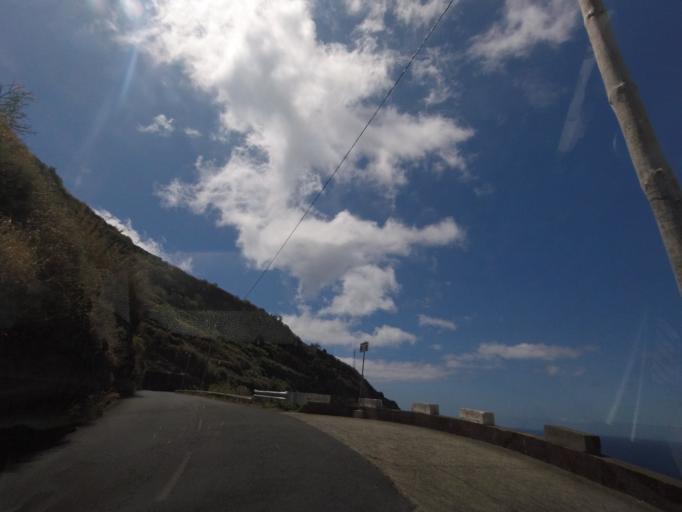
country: PT
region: Madeira
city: Ponta do Sol
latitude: 32.6869
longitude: -17.0828
